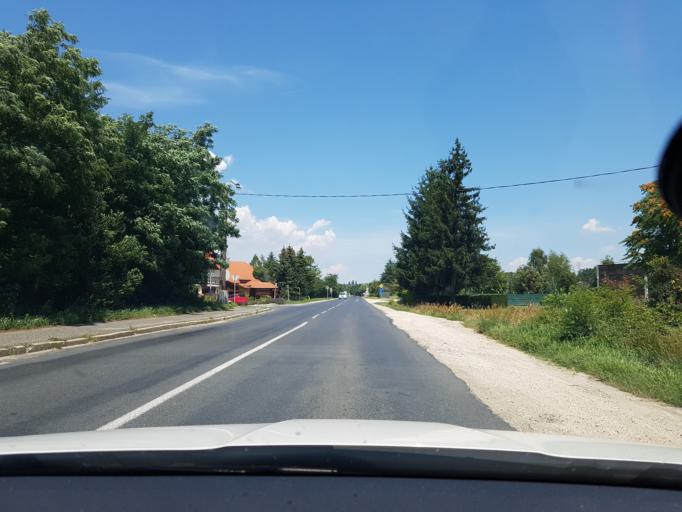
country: HU
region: Vas
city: Koszeg
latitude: 47.3855
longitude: 16.5546
